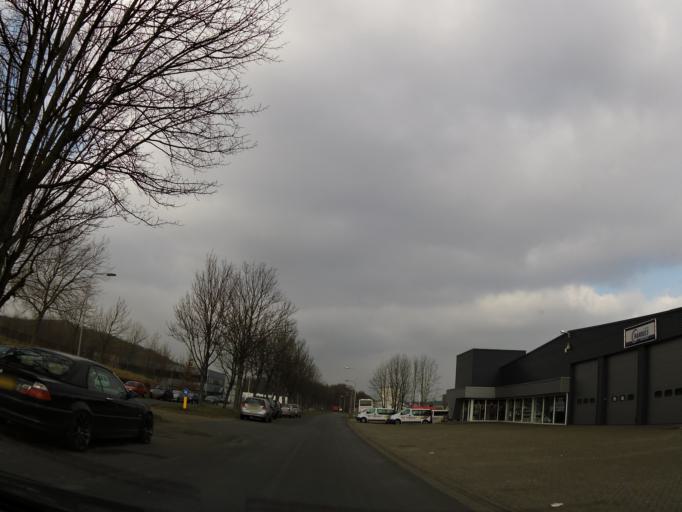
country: NL
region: Limburg
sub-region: Gemeente Kerkrade
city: Kerkrade
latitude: 50.8685
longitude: 6.0323
